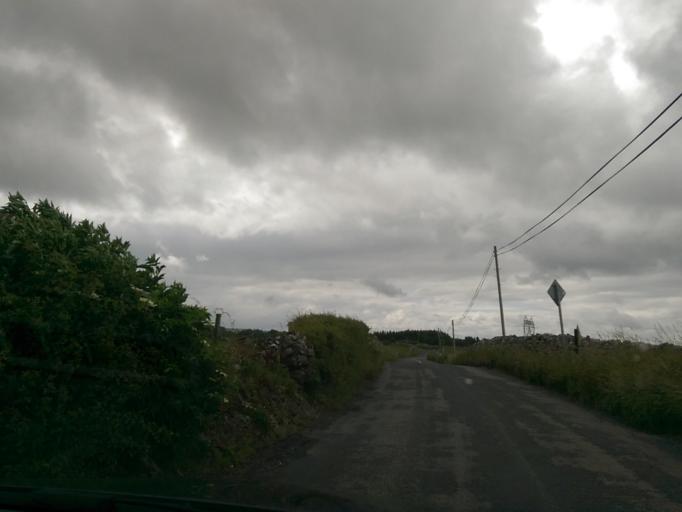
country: IE
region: Connaught
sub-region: County Galway
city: Loughrea
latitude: 53.2274
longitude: -8.5592
